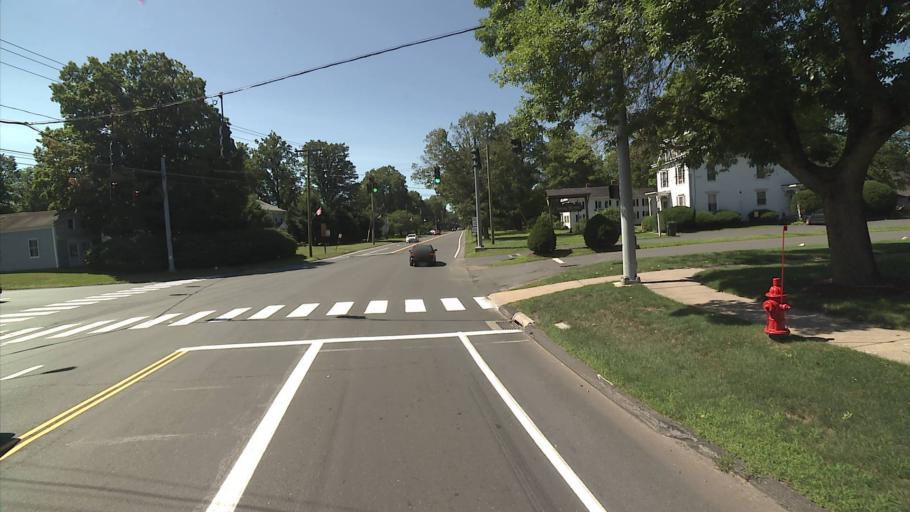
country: US
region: Connecticut
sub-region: Hartford County
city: Salmon Brook
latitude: 41.9530
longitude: -72.7894
